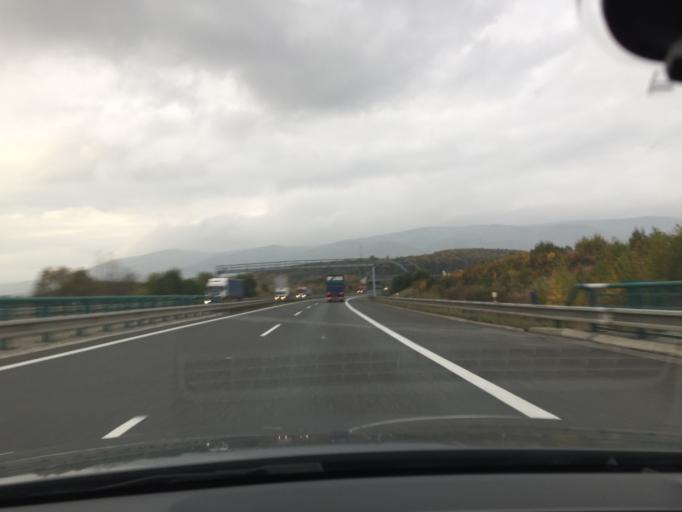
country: CZ
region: Ustecky
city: Chabarovice
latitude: 50.6728
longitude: 13.9674
